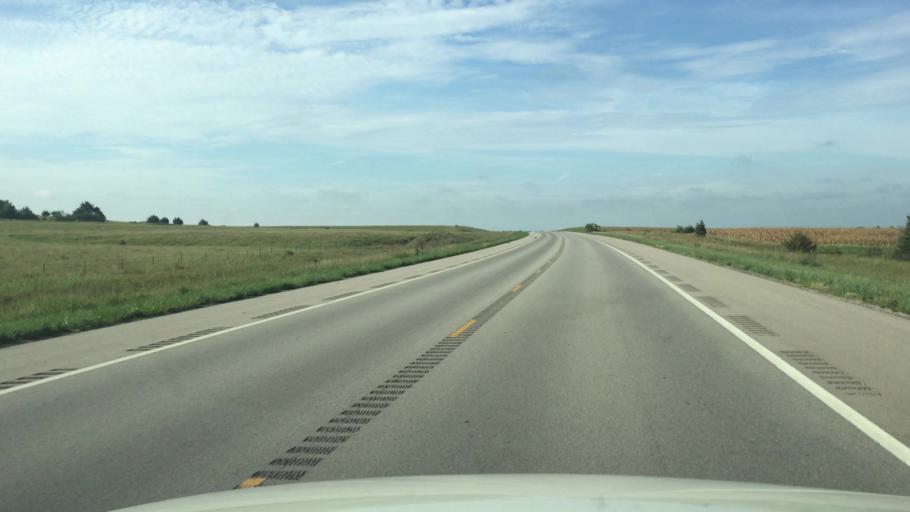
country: US
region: Kansas
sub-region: Allen County
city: Iola
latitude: 38.0641
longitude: -95.3786
